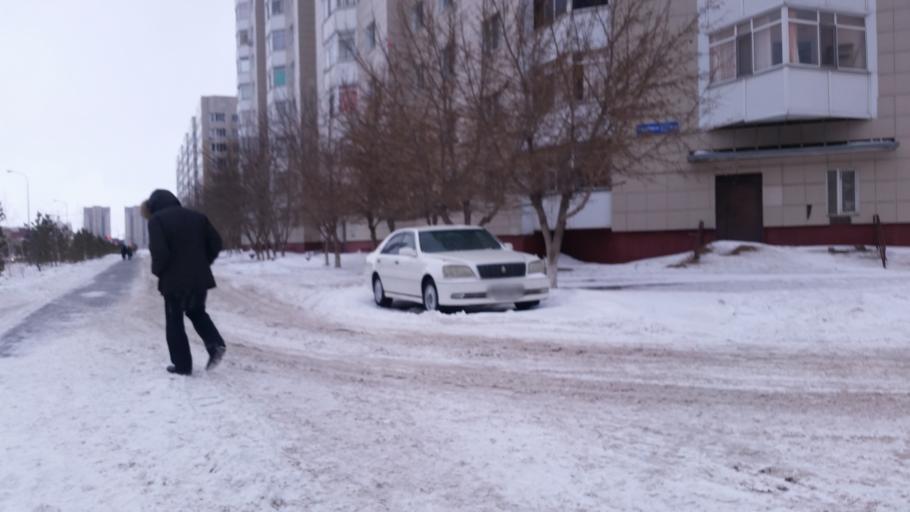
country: KZ
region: Astana Qalasy
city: Astana
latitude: 51.1155
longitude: 71.4175
